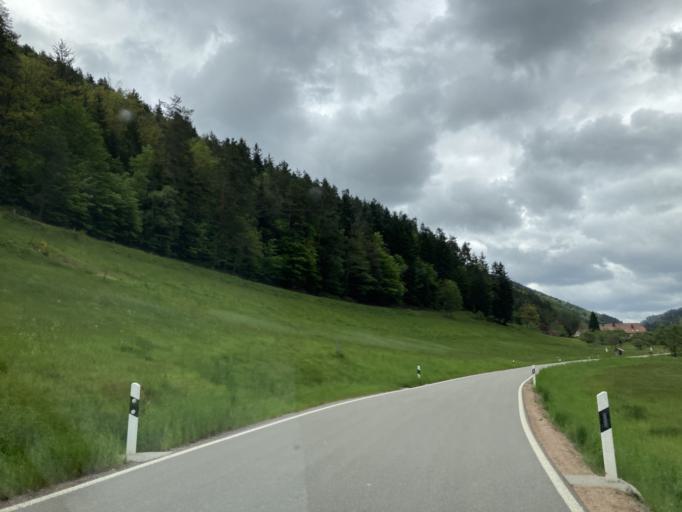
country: DE
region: Baden-Wuerttemberg
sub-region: Freiburg Region
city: Schonach im Schwarzwald
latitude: 48.1979
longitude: 8.1610
